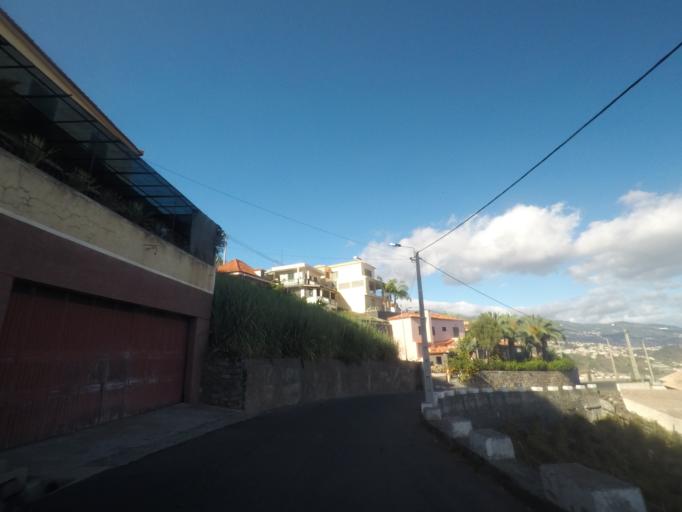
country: PT
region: Madeira
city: Camara de Lobos
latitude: 32.6642
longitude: -16.9929
